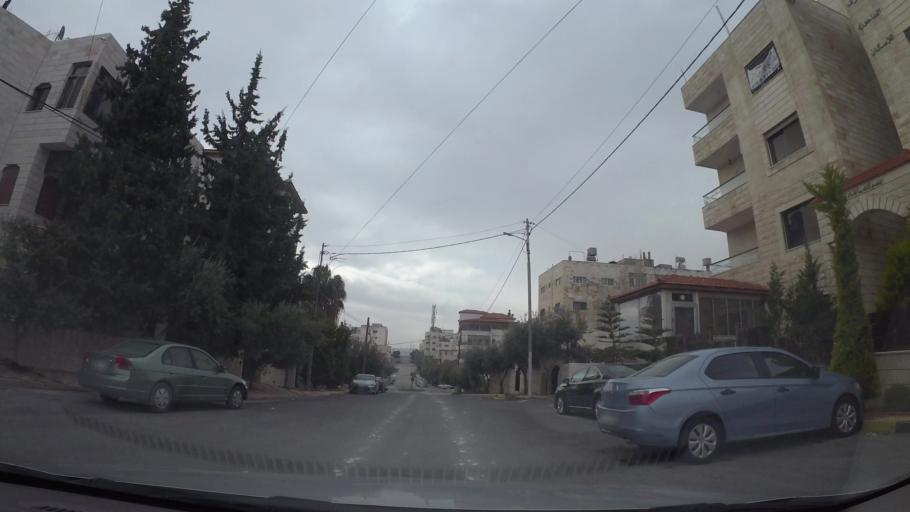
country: JO
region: Amman
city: Umm as Summaq
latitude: 31.9053
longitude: 35.8481
